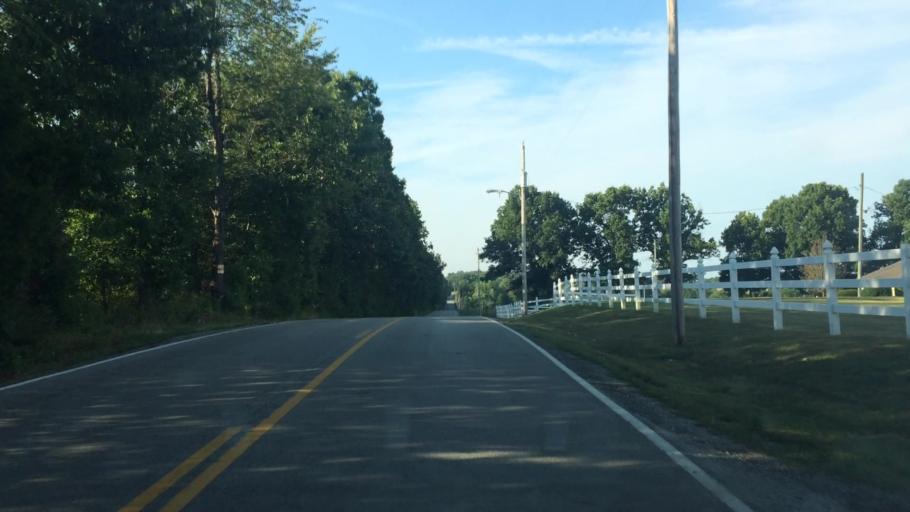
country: US
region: Missouri
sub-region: Greene County
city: Strafford
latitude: 37.2645
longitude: -93.1877
